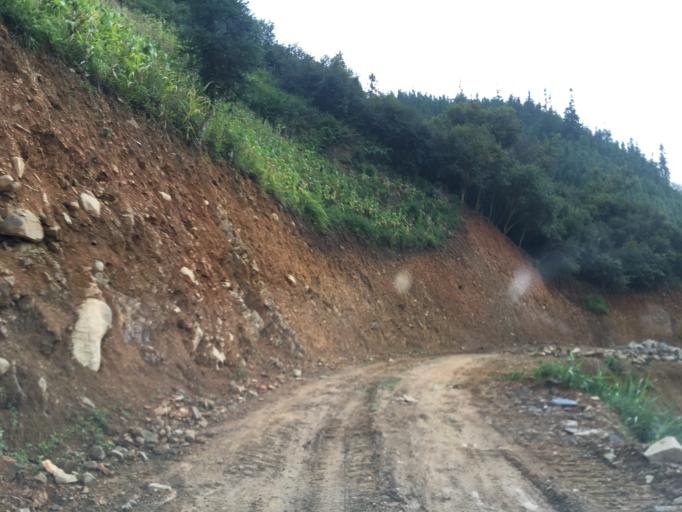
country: CN
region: Guangxi Zhuangzu Zizhiqu
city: Xinzhou
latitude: 24.8690
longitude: 105.8660
